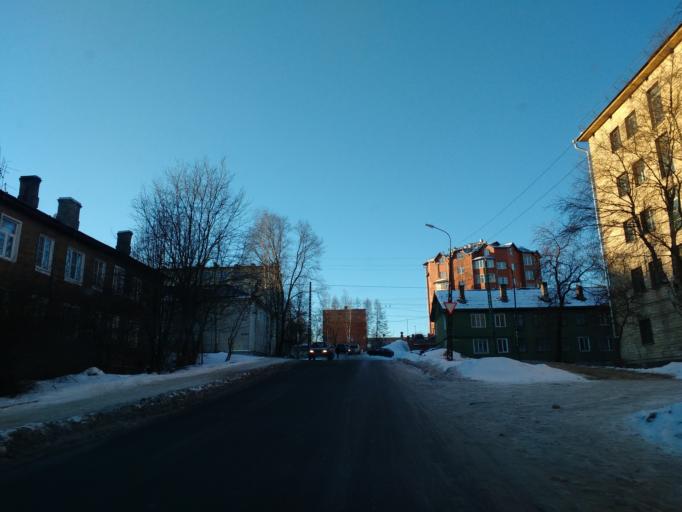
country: RU
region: Republic of Karelia
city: Petrozavodsk
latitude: 61.7767
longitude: 34.3810
